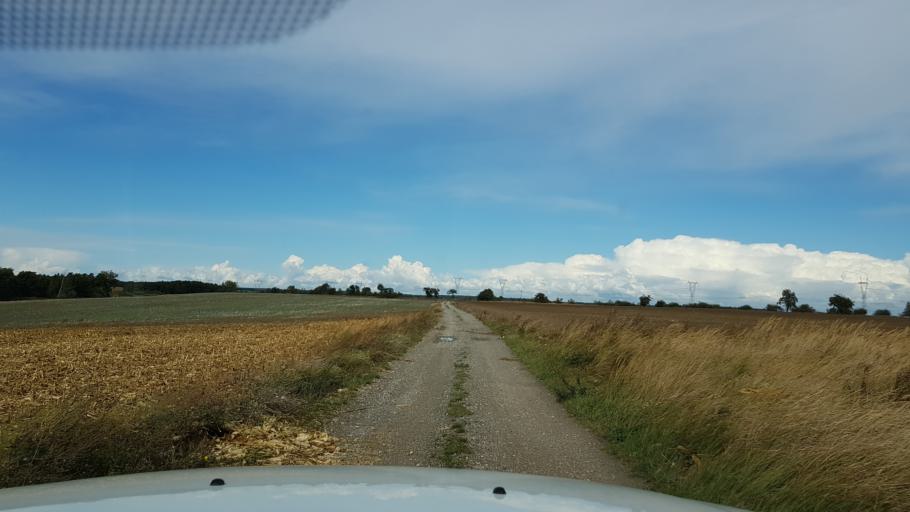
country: PL
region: West Pomeranian Voivodeship
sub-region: Powiat gryfinski
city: Banie
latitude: 53.1126
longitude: 14.6540
